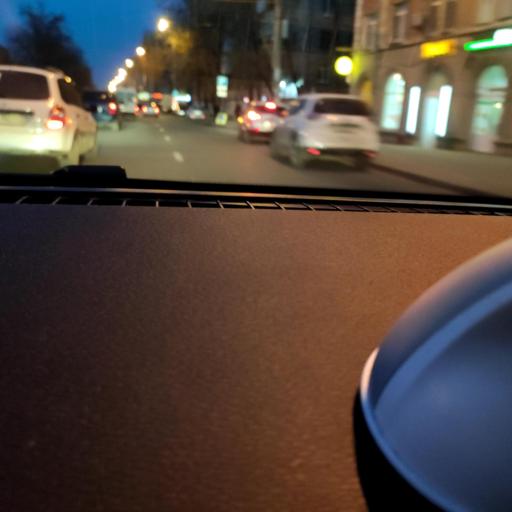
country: RU
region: Samara
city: Samara
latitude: 53.2135
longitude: 50.2504
